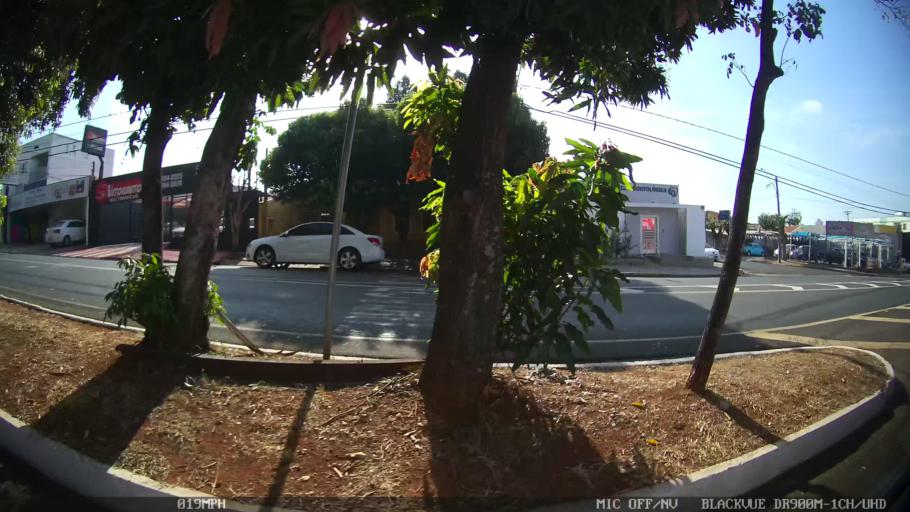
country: BR
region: Sao Paulo
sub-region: Sao Jose Do Rio Preto
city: Sao Jose do Rio Preto
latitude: -20.8003
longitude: -49.4088
